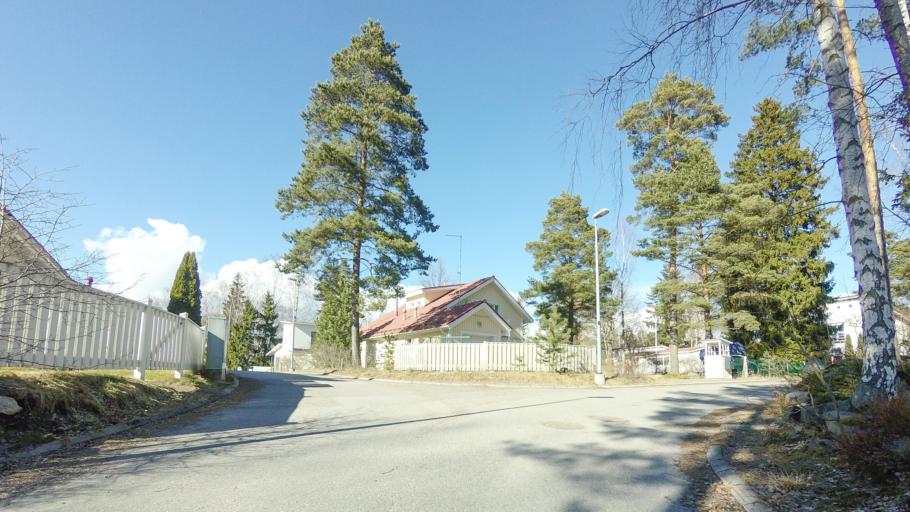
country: FI
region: Uusimaa
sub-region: Helsinki
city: Vantaa
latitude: 60.1665
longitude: 25.0770
